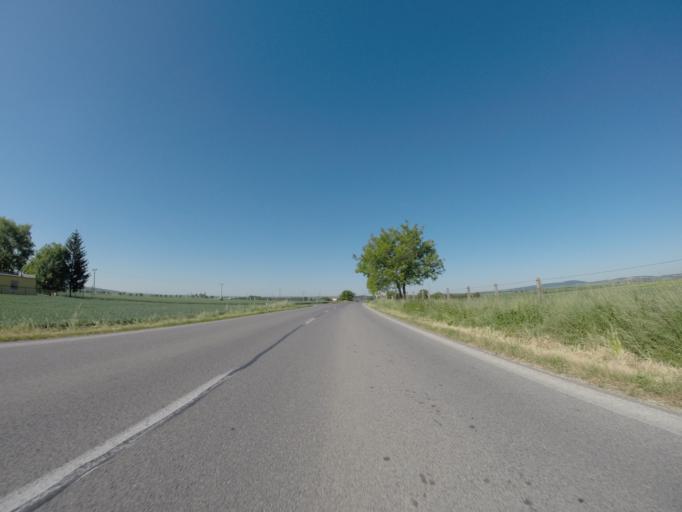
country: SK
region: Trnavsky
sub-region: Okres Trnava
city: Piestany
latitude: 48.5112
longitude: 17.9924
